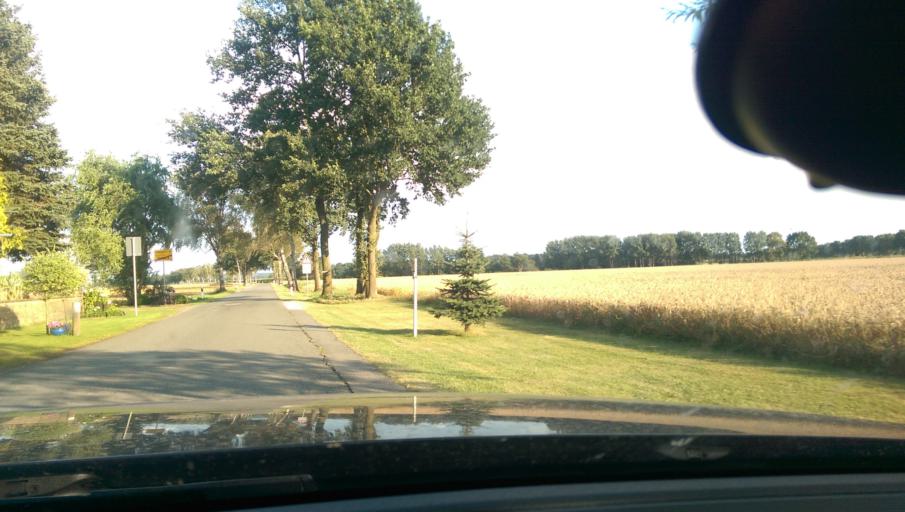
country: DE
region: Lower Saxony
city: Lindwedel
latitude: 52.5994
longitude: 9.6140
